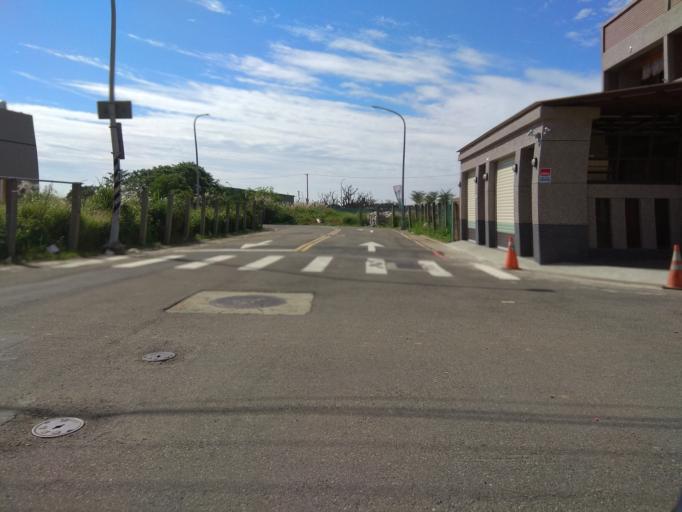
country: TW
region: Taiwan
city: Taoyuan City
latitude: 25.0434
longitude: 121.1345
